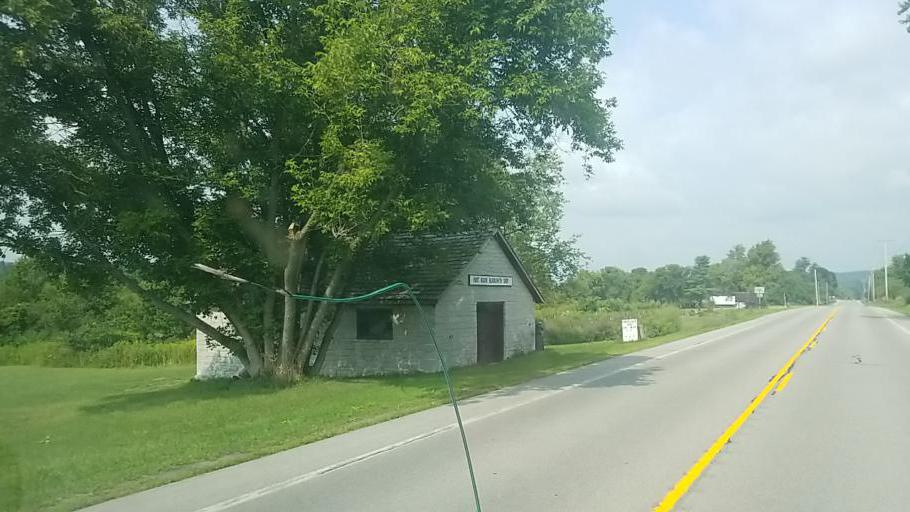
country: US
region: New York
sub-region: Montgomery County
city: Saint Johnsville
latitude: 42.9862
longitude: -74.6484
